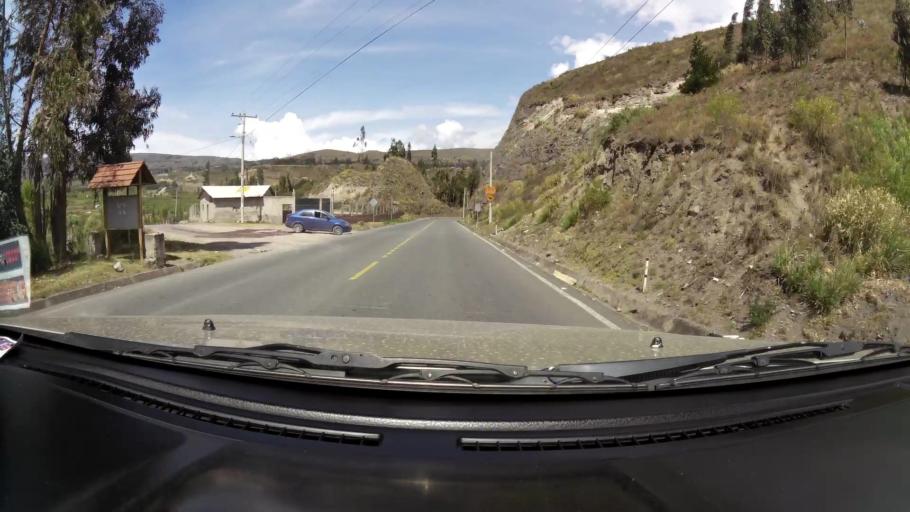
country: EC
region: Chimborazo
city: Guano
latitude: -1.6364
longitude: -78.5968
